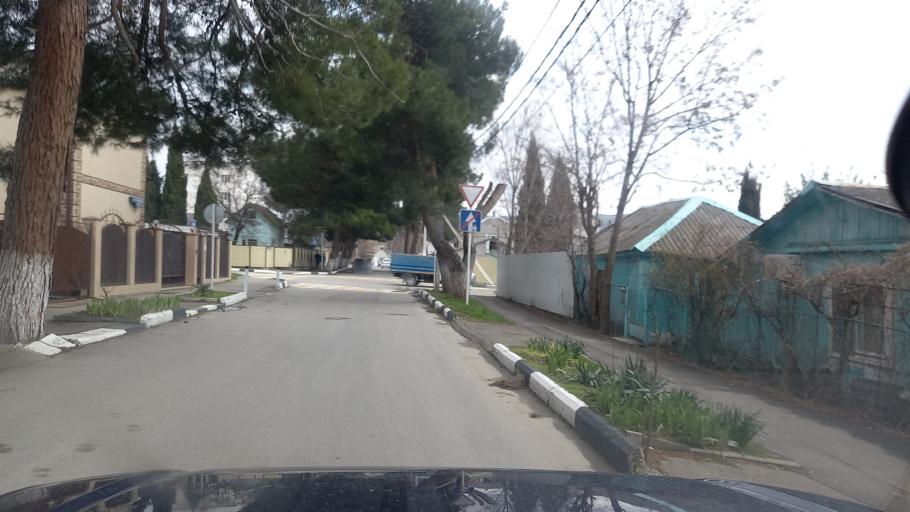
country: RU
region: Krasnodarskiy
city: Gelendzhik
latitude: 44.5596
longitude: 38.0869
